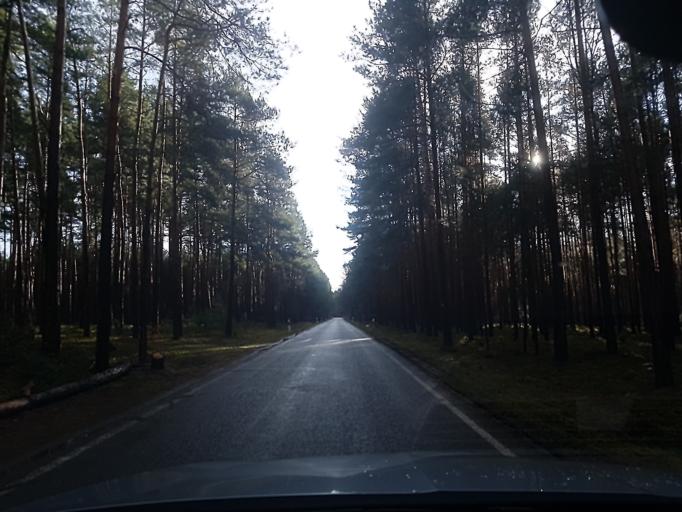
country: DE
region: Brandenburg
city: Schilda
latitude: 51.5768
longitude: 13.3255
